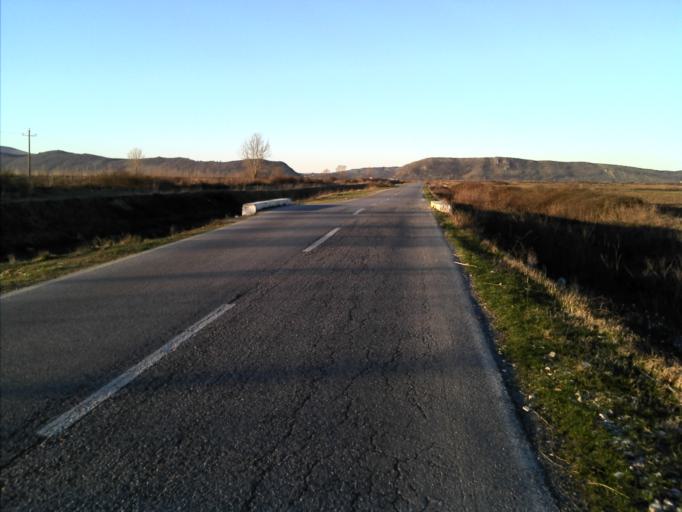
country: AL
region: Shkoder
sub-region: Rrethi i Shkodres
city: Dajc
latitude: 41.9575
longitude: 19.4602
